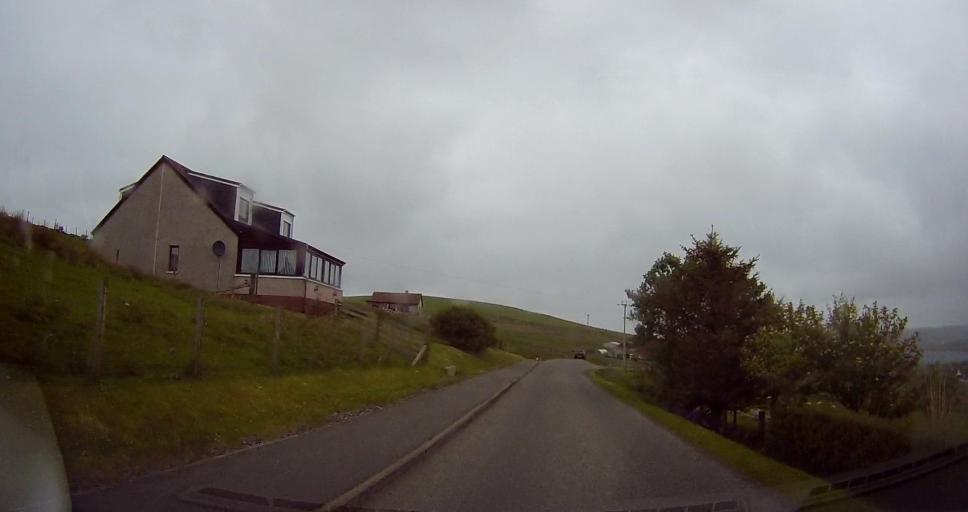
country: GB
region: Scotland
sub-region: Shetland Islands
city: Lerwick
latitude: 60.2806
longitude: -1.3886
